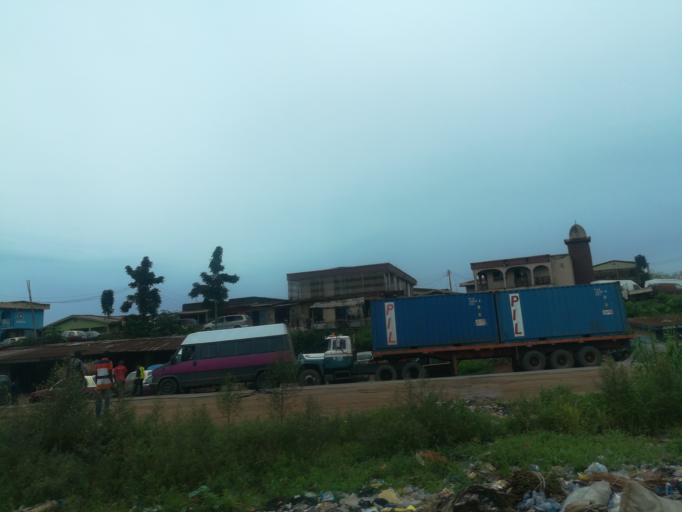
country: NG
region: Oyo
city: Ibadan
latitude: 7.3451
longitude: 3.9184
